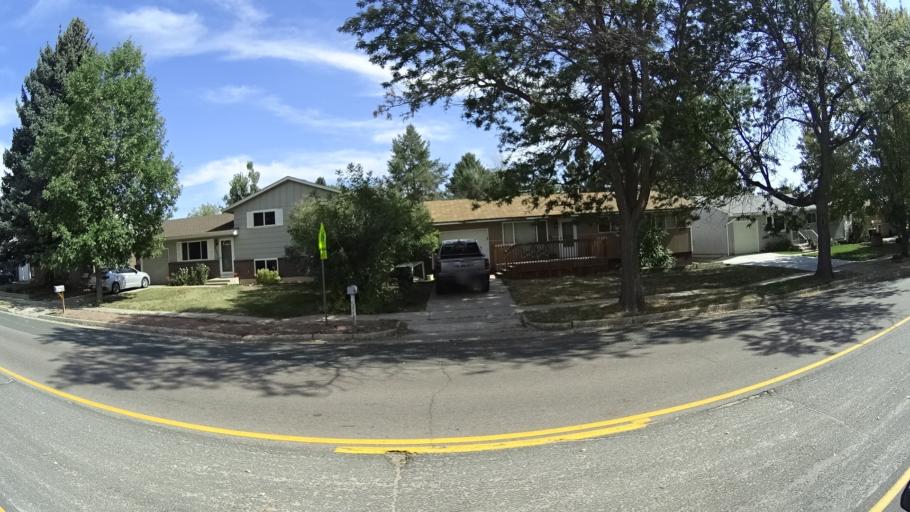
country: US
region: Colorado
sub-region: El Paso County
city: Cimarron Hills
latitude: 38.8941
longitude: -104.7657
